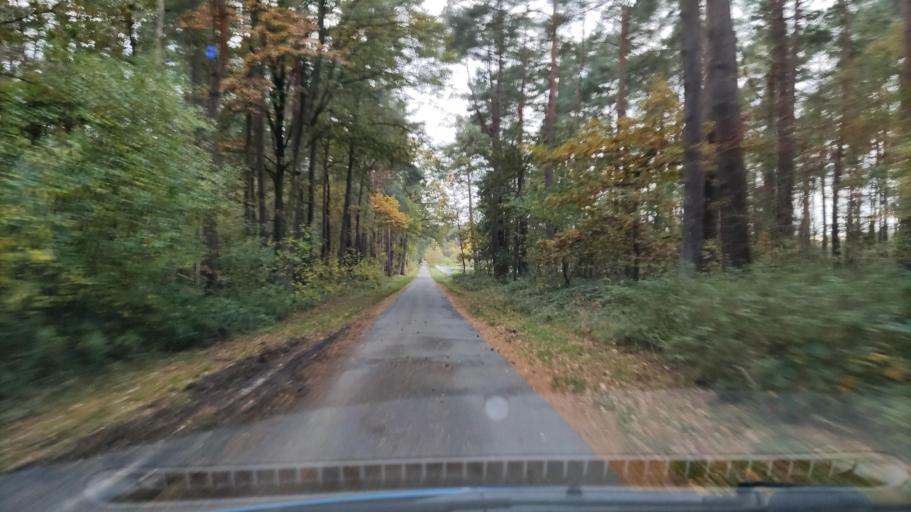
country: DE
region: Lower Saxony
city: Hitzacker
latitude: 53.1298
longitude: 11.0010
